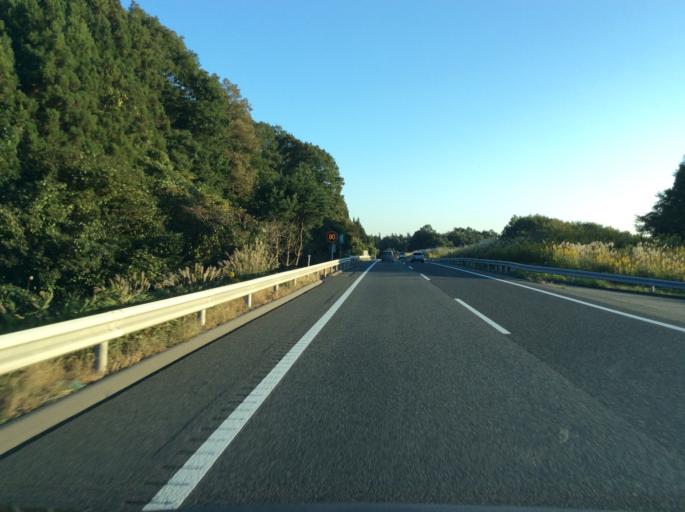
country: JP
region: Fukushima
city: Funehikimachi-funehiki
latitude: 37.3456
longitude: 140.6087
